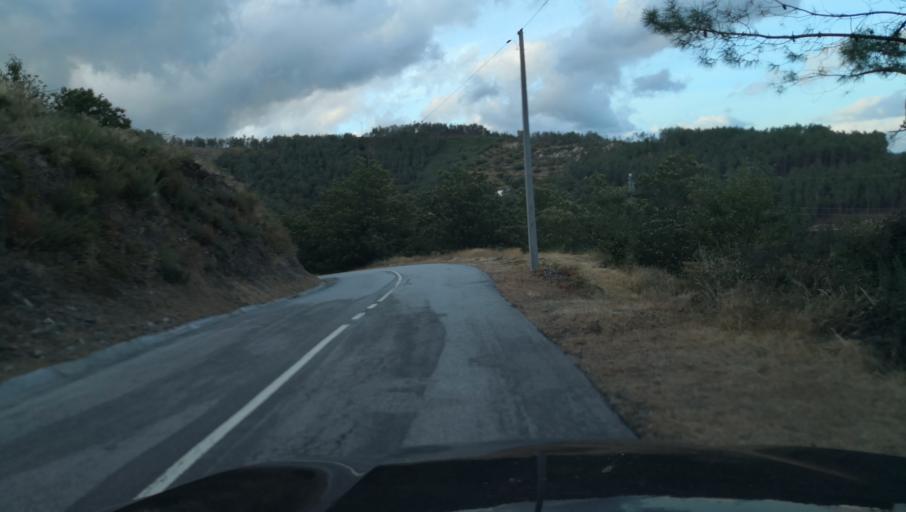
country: PT
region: Vila Real
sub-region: Santa Marta de Penaguiao
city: Santa Marta de Penaguiao
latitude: 41.2397
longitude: -7.8504
